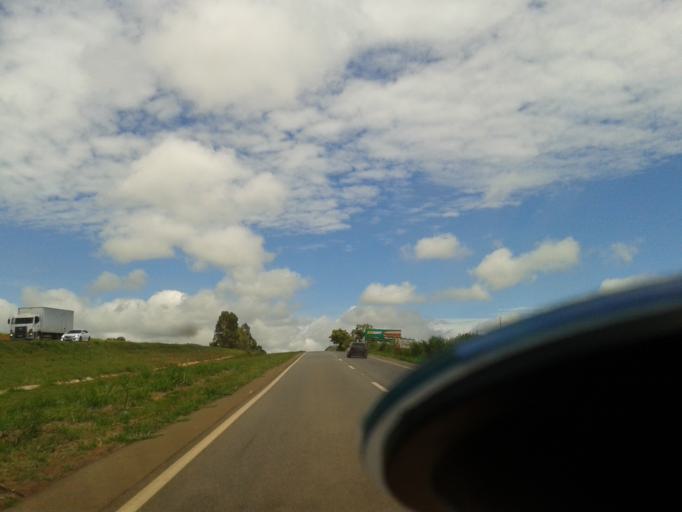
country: BR
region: Goias
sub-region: Inhumas
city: Inhumas
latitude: -16.2265
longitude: -49.5619
